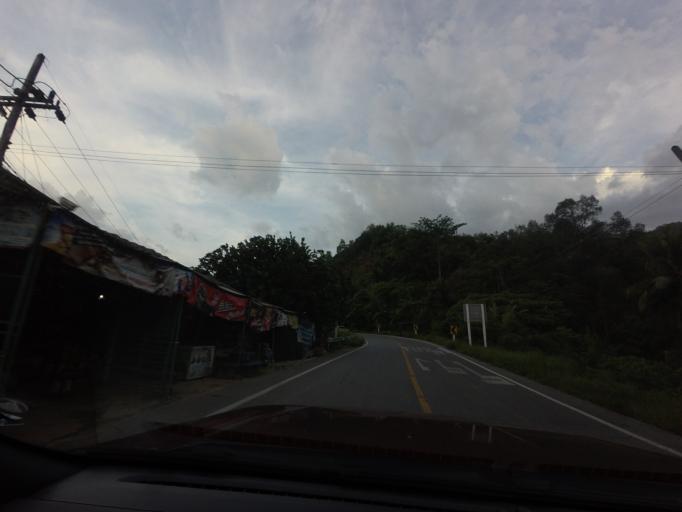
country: TH
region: Yala
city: Than To
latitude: 6.0184
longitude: 101.2002
